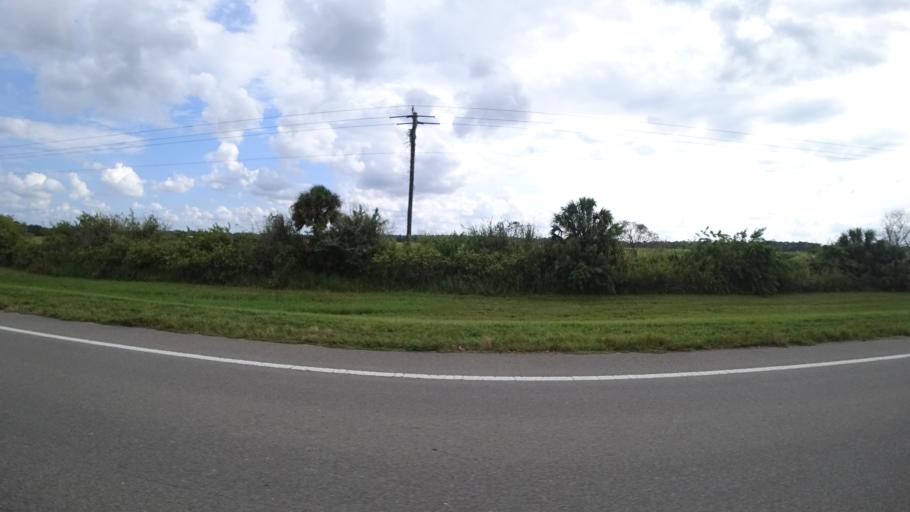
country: US
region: Florida
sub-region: Hillsborough County
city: Sun City Center
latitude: 27.5940
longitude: -82.3681
